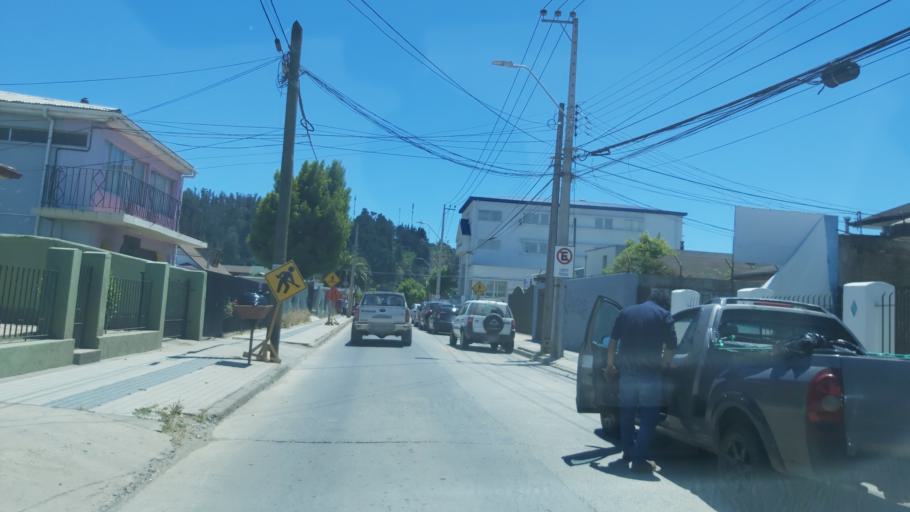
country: CL
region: Maule
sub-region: Provincia de Talca
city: Constitucion
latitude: -35.3290
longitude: -72.4082
